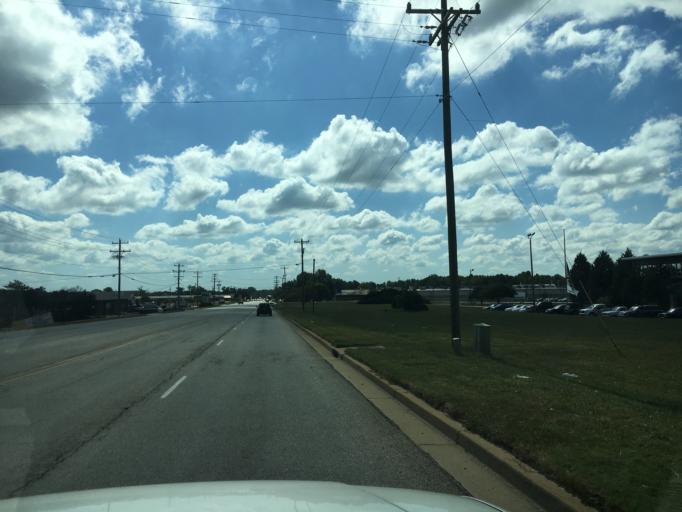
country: US
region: South Carolina
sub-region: Greenville County
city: Greer
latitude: 34.9379
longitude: -82.2557
